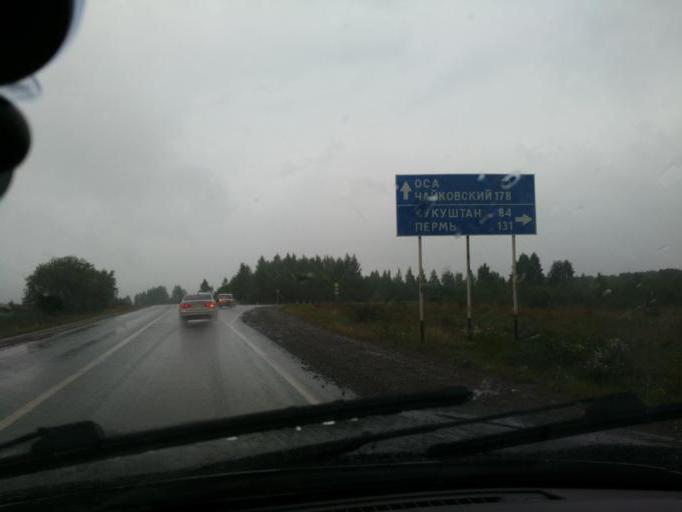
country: RU
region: Perm
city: Osa
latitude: 57.1774
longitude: 55.5318
